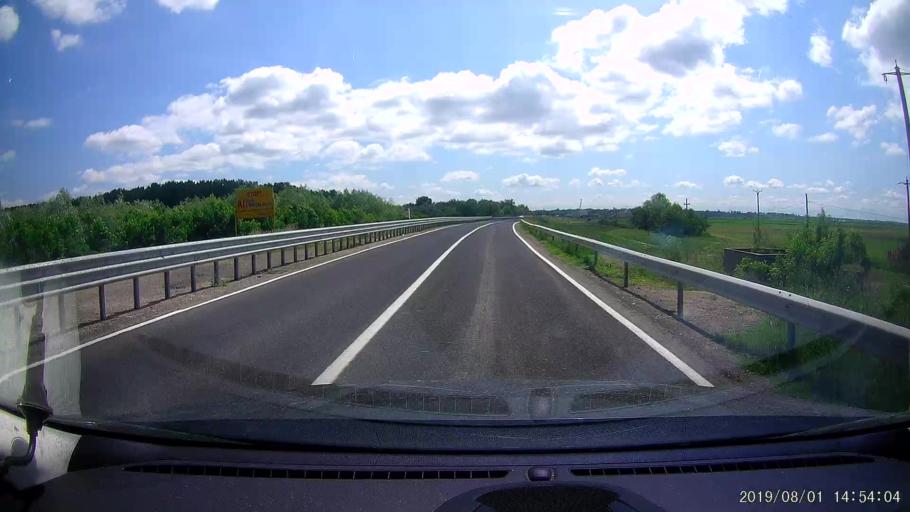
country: RO
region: Braila
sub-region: Municipiul Braila
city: Braila
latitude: 45.3238
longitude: 27.9950
